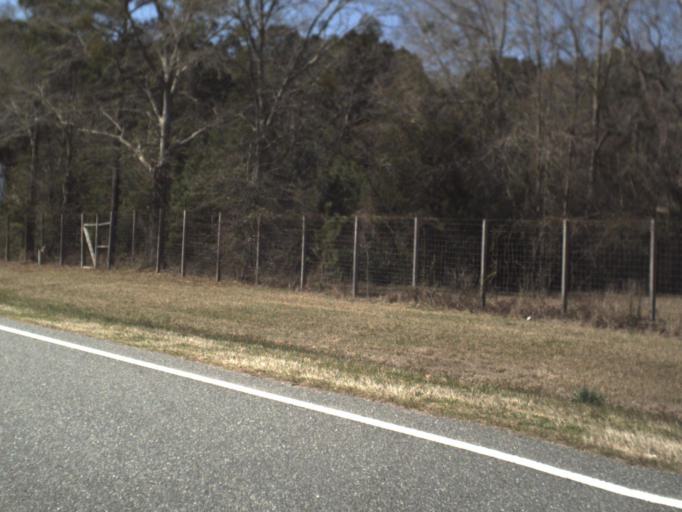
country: US
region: Florida
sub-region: Jackson County
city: Marianna
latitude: 30.7521
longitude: -85.2756
